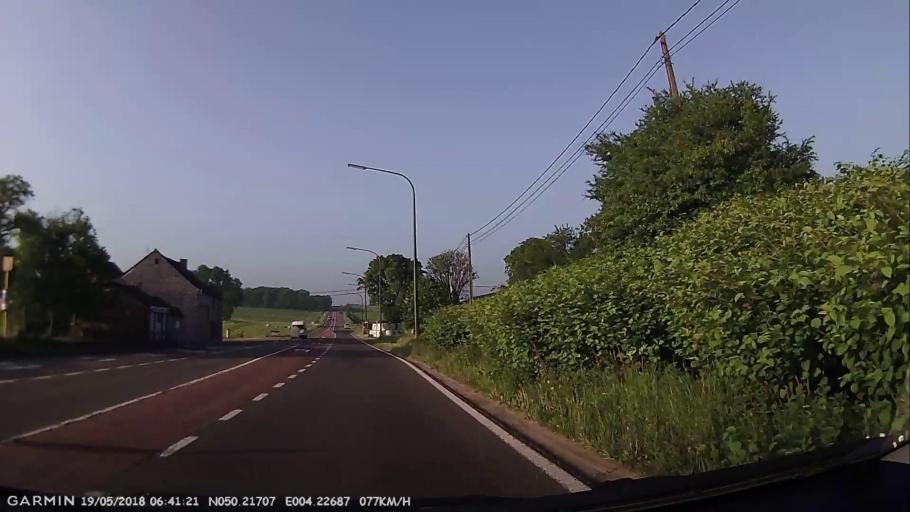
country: BE
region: Wallonia
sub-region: Province du Hainaut
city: Beaumont
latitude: 50.2168
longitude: 4.2268
